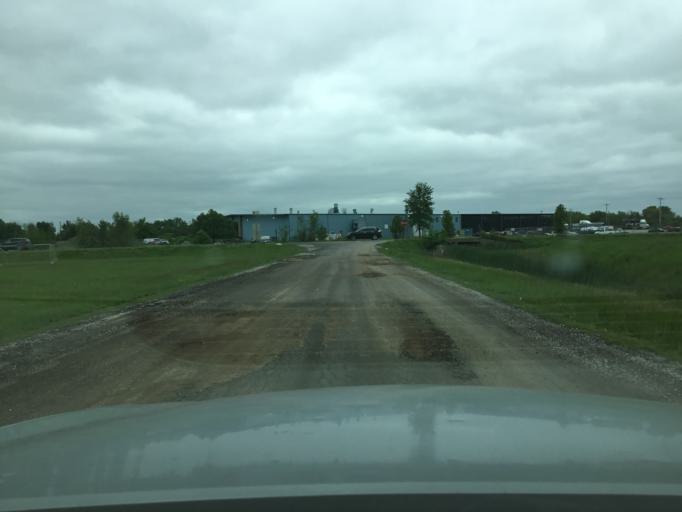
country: US
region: Kansas
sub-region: Franklin County
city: Ottawa
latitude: 38.6369
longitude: -95.2585
